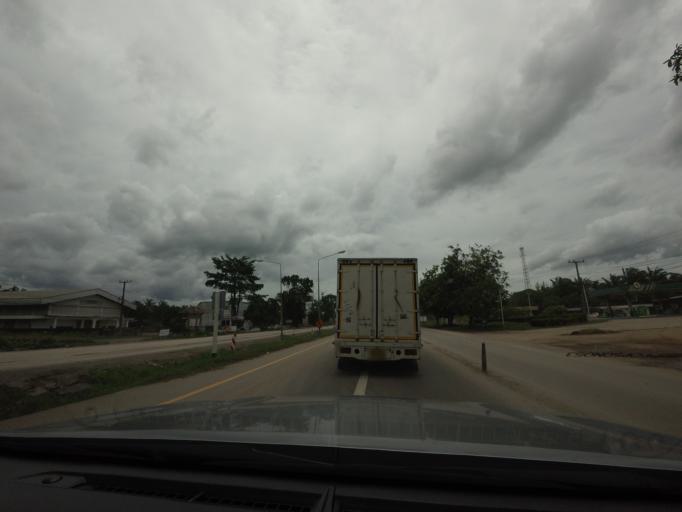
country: TH
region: Chumphon
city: Lamae
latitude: 9.7587
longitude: 99.0845
